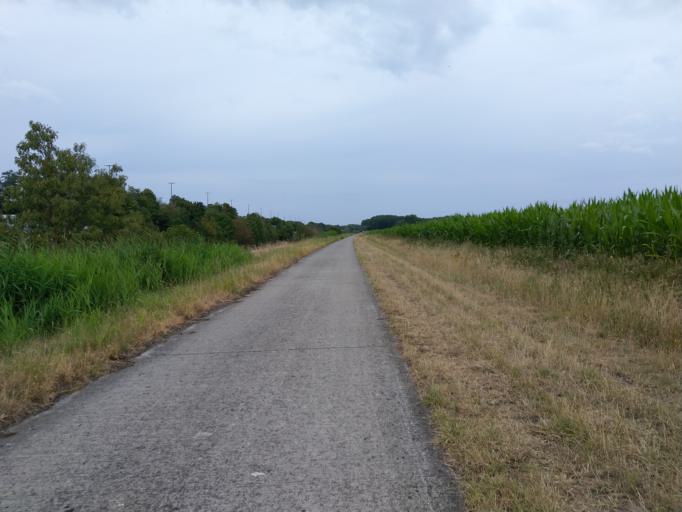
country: BE
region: Wallonia
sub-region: Province du Hainaut
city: Boussu
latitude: 50.4518
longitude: 3.7526
